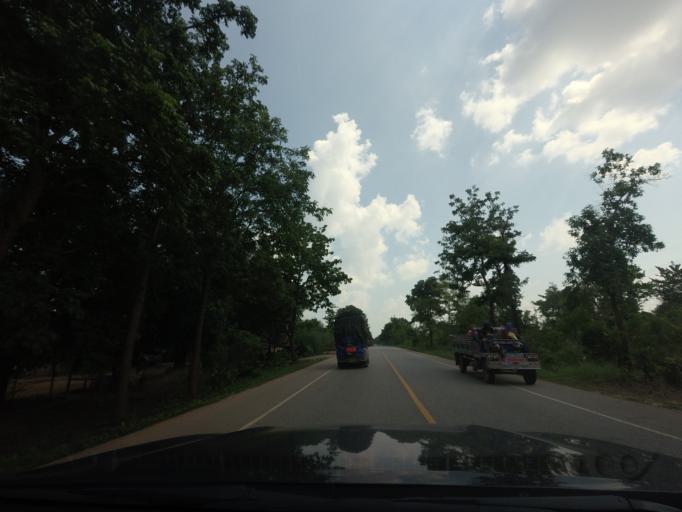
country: TH
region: Phitsanulok
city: Chat Trakan
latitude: 17.2783
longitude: 100.5388
